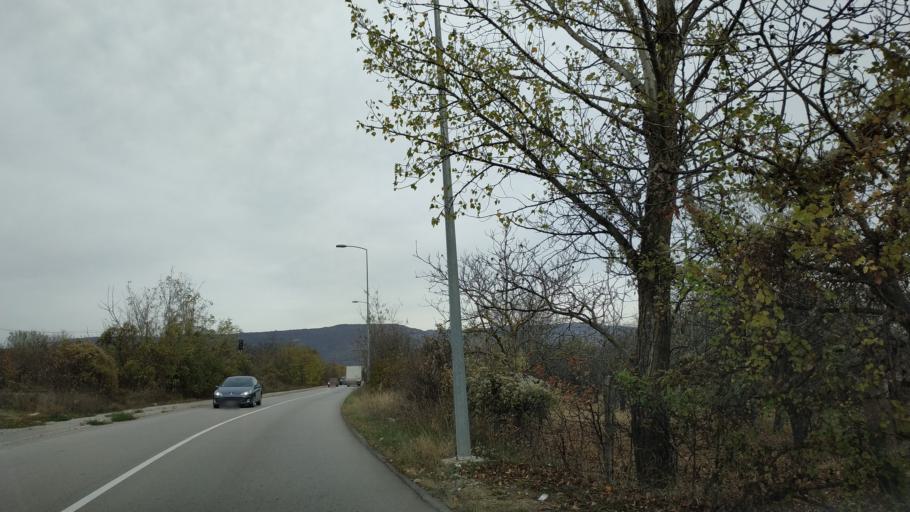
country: RS
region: Central Serbia
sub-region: Nisavski Okrug
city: Nis
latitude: 43.3464
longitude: 21.9366
